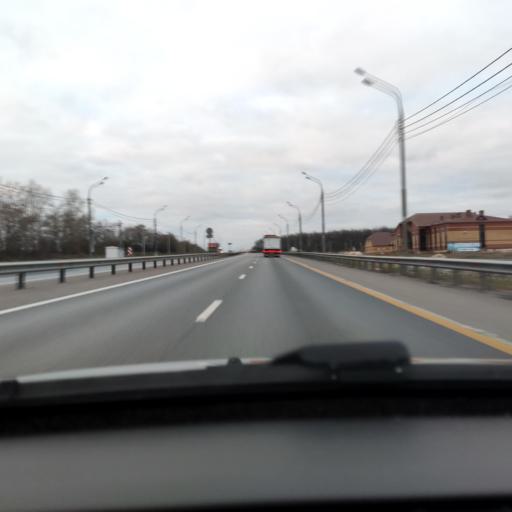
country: RU
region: Lipetsk
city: Khlevnoye
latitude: 52.1435
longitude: 39.2004
